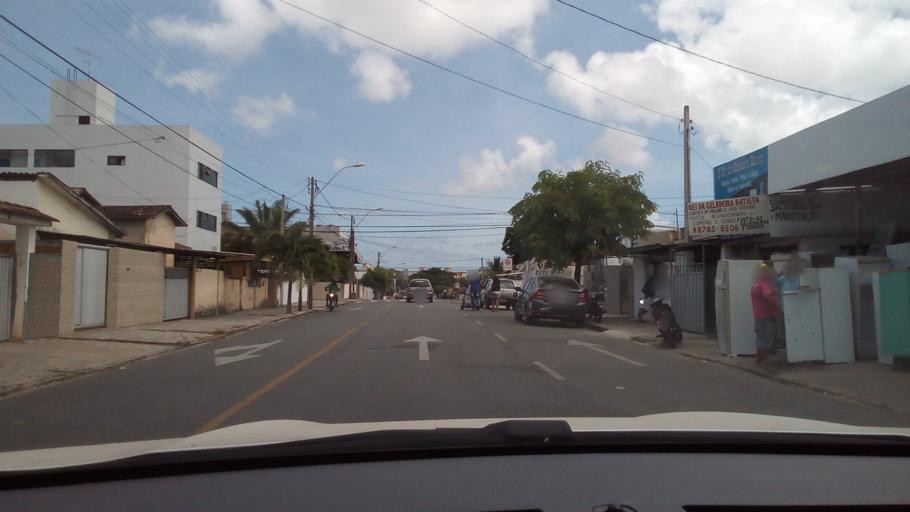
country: BR
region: Paraiba
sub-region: Joao Pessoa
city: Joao Pessoa
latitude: -7.1246
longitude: -34.8622
